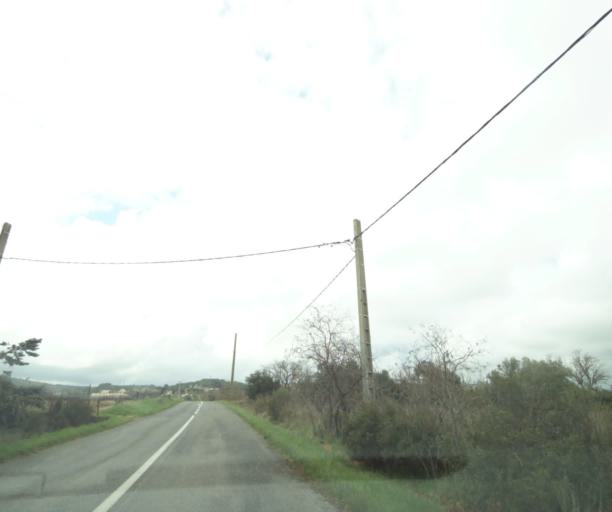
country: FR
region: Languedoc-Roussillon
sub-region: Departement de l'Herault
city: Murviel-les-Montpellier
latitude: 43.5990
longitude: 3.7430
